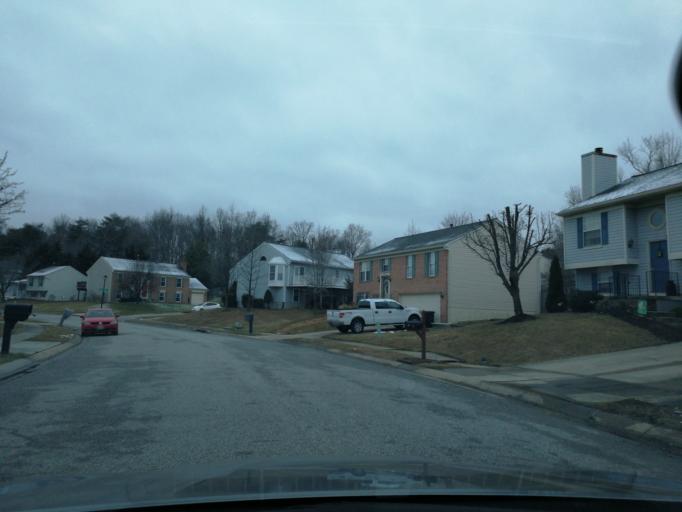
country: US
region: Maryland
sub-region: Harford County
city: Bel Air South
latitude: 39.4663
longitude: -76.2960
